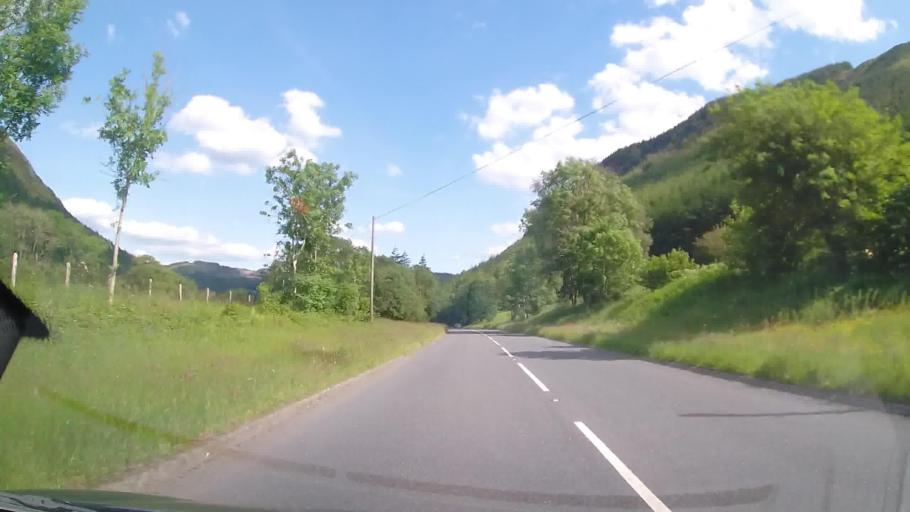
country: GB
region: Wales
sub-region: Gwynedd
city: Corris
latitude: 52.7246
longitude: -3.7072
